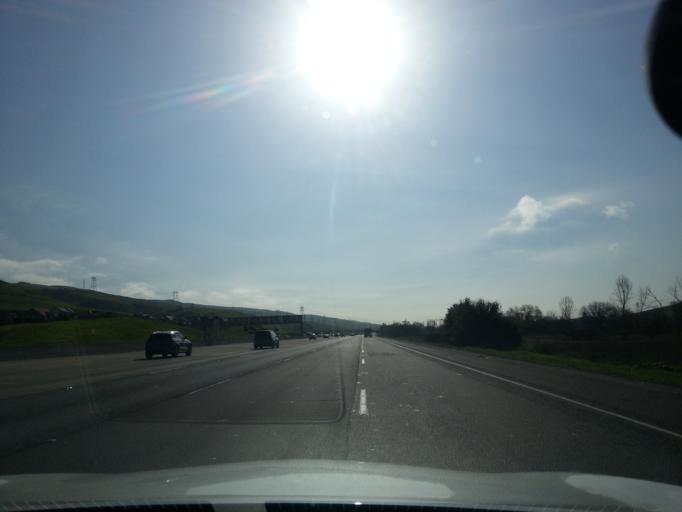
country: US
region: California
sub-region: Santa Clara County
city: Seven Trees
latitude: 37.2351
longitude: -121.7576
